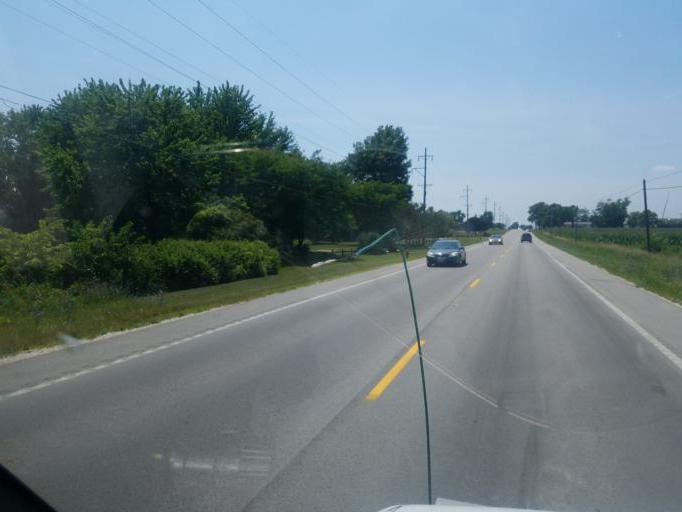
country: US
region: Ohio
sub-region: Mercer County
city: Celina
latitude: 40.5506
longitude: -84.4994
